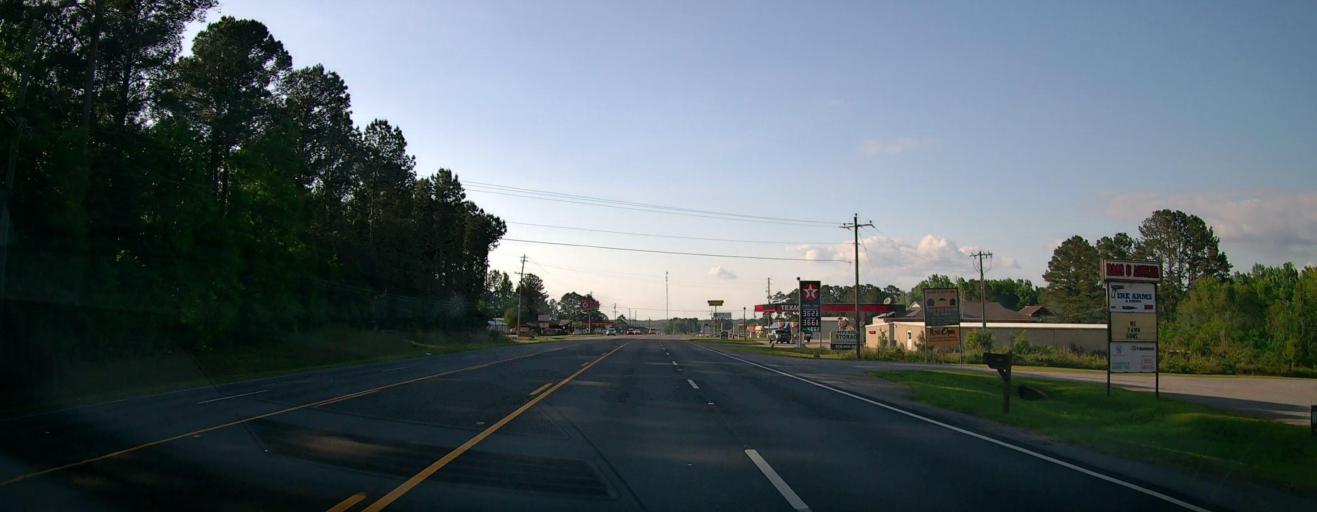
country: US
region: Georgia
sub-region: Baldwin County
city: Milledgeville
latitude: 33.1813
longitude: -83.2887
